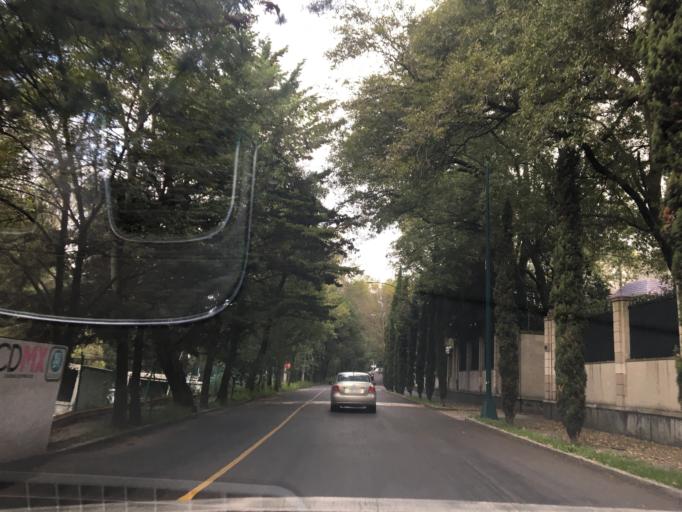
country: MX
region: Mexico City
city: Polanco
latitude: 19.4163
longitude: -99.2099
